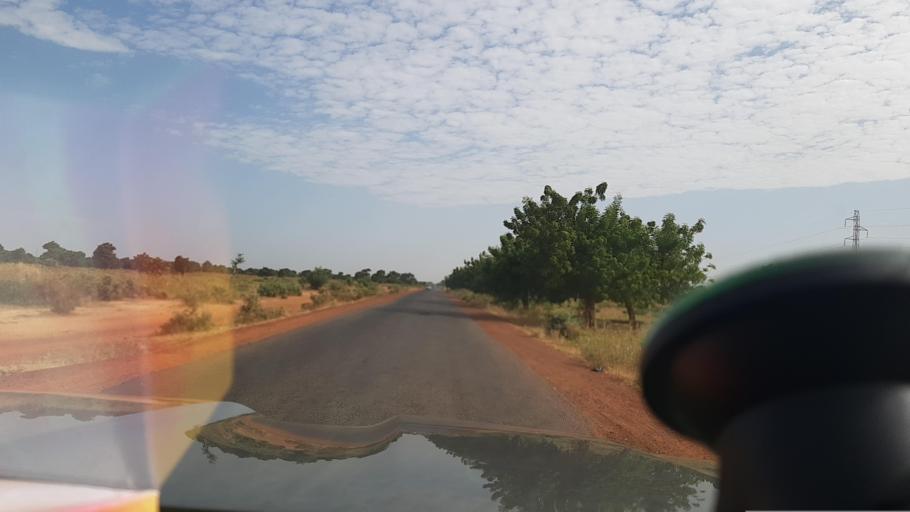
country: ML
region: Segou
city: Segou
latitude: 13.5065
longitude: -6.1461
